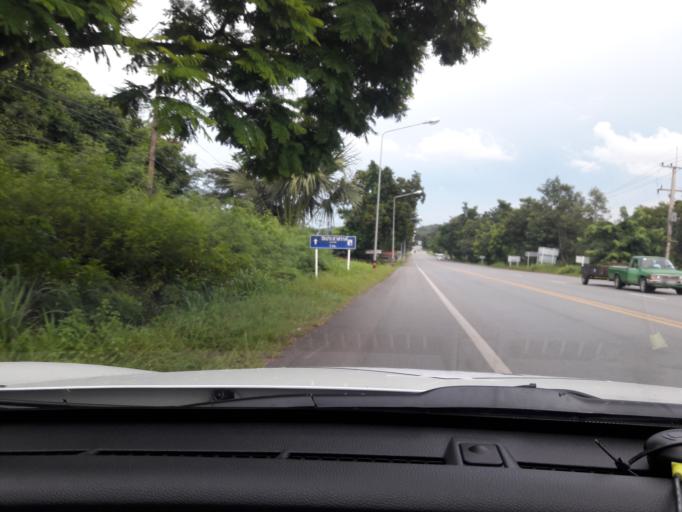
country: TH
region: Nakhon Sawan
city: Tak Fa
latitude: 15.3538
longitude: 100.5073
